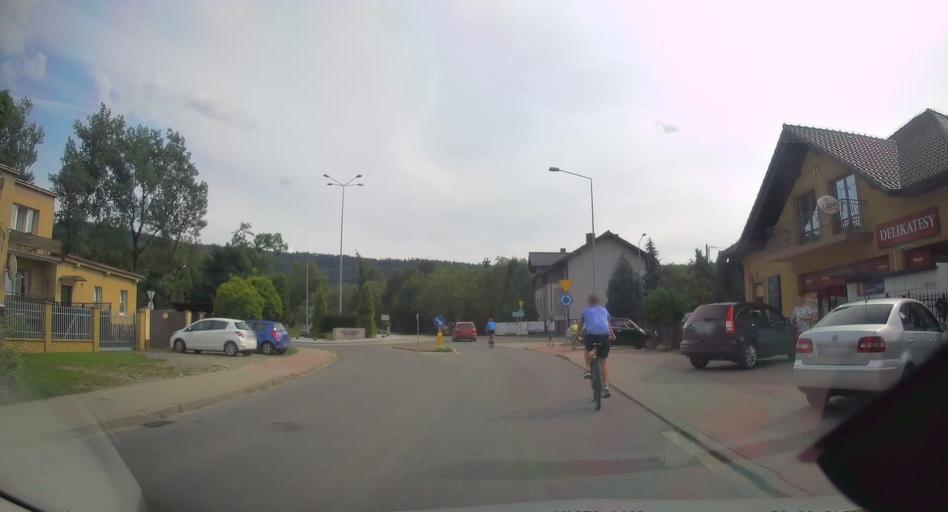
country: PL
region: Lesser Poland Voivodeship
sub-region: Powiat myslenicki
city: Myslenice
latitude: 49.8252
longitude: 19.9439
